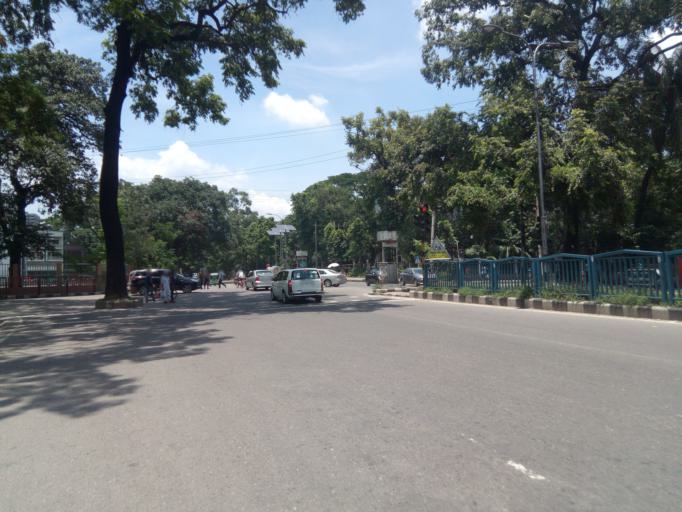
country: BD
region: Dhaka
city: Paltan
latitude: 23.7414
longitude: 90.4056
